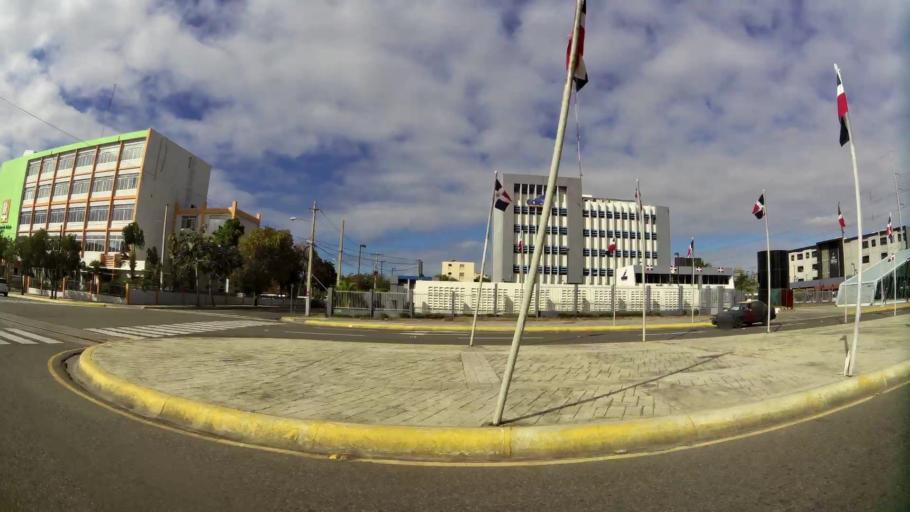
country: DO
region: Nacional
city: La Julia
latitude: 18.4505
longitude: -69.9271
